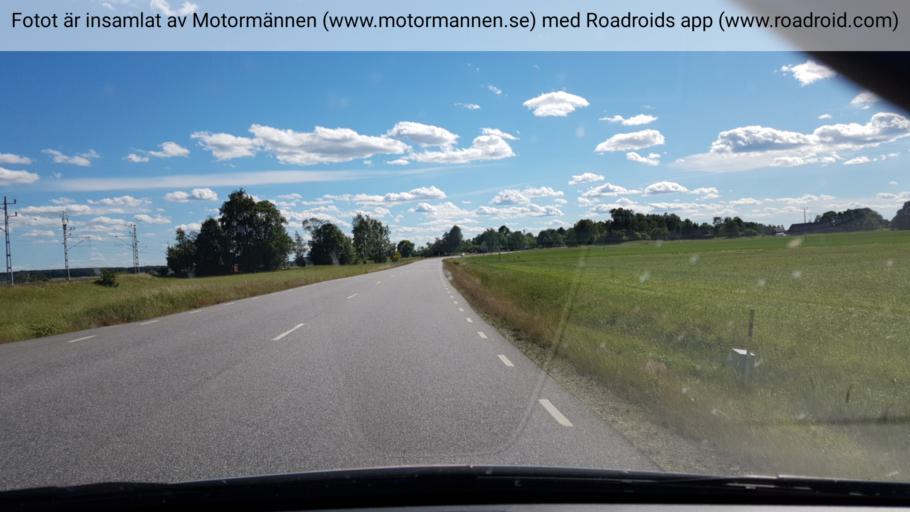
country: SE
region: Vaestra Goetaland
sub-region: Toreboda Kommun
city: Toereboda
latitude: 58.6484
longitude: 14.0761
